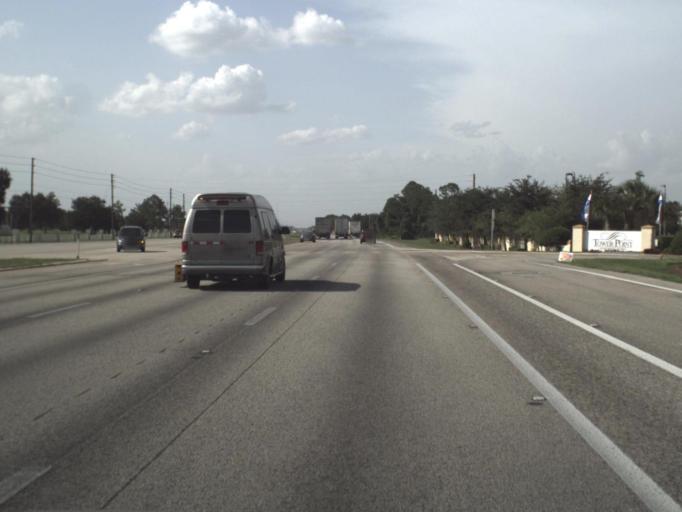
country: US
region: Florida
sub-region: Polk County
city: Lake Wales
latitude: 27.9319
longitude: -81.6086
